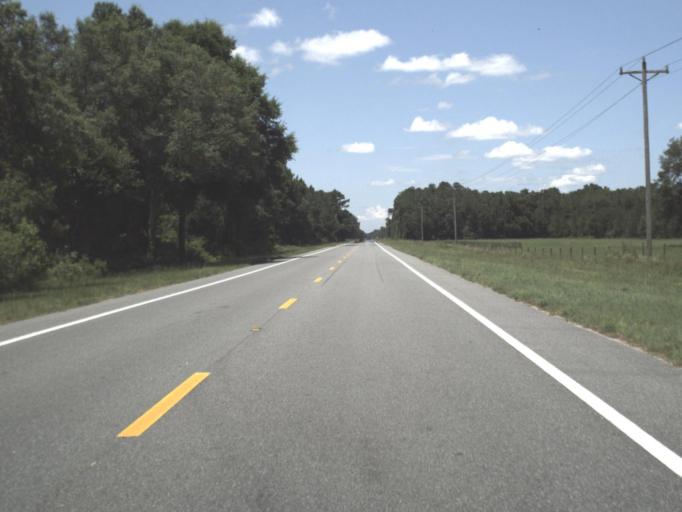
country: US
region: Florida
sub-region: Lafayette County
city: Mayo
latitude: 29.9002
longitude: -82.9535
